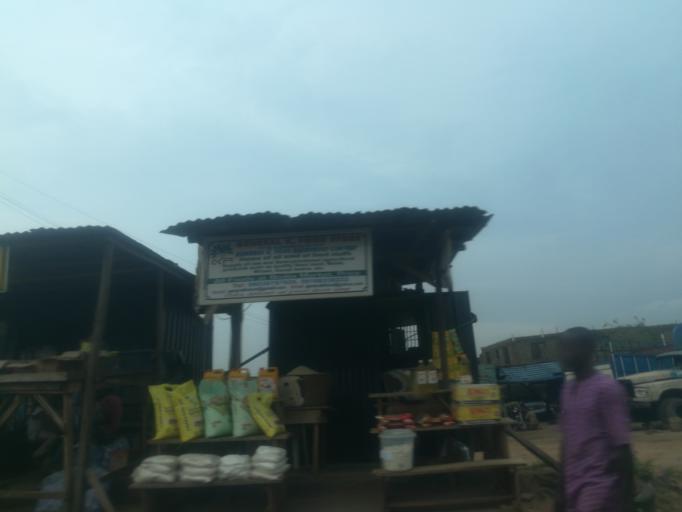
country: NG
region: Oyo
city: Ibadan
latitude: 7.4381
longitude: 3.9247
